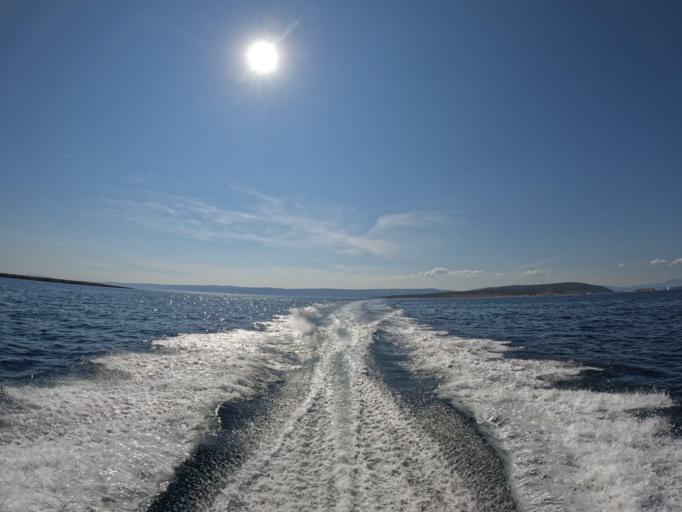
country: HR
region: Primorsko-Goranska
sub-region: Grad Krk
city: Krk
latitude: 44.9541
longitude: 14.5734
